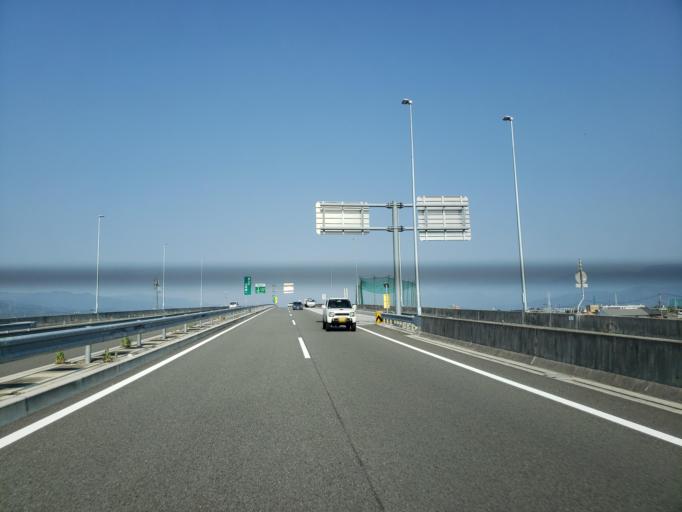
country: JP
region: Ehime
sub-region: Shikoku-chuo Shi
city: Matsuyama
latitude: 33.8024
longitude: 132.7699
